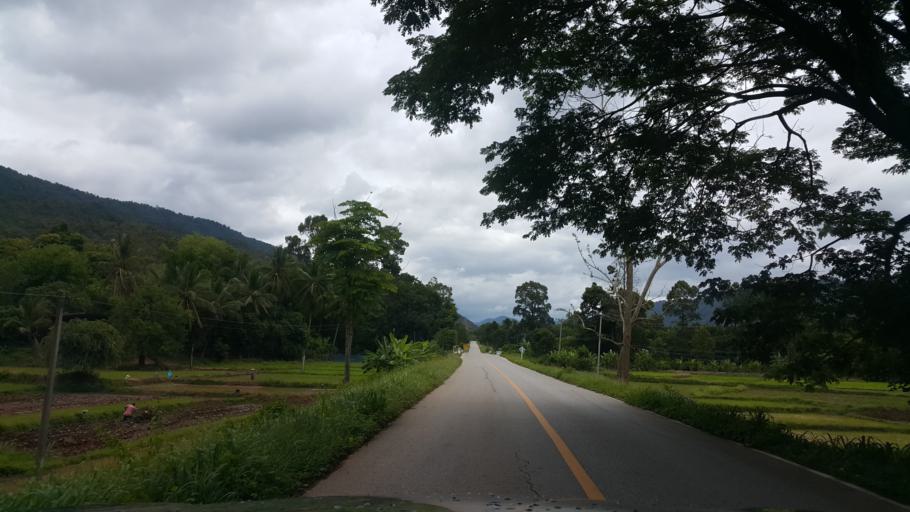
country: TH
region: Phitsanulok
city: Chat Trakan
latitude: 17.3306
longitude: 100.7018
